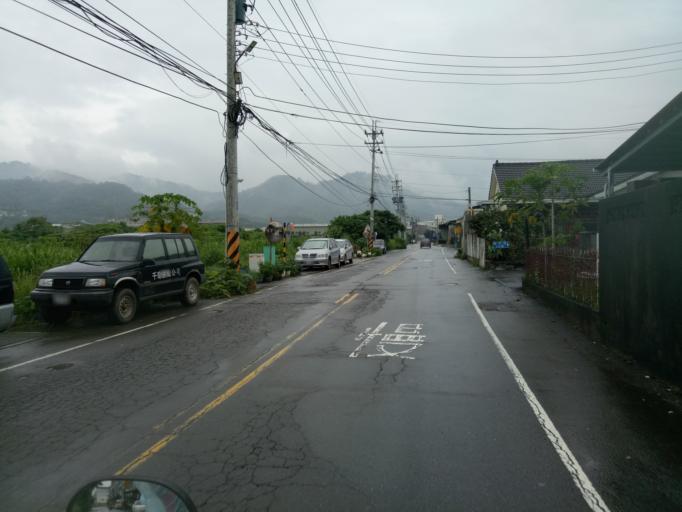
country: TW
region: Taiwan
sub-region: Taichung City
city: Taichung
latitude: 24.0991
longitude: 120.7246
